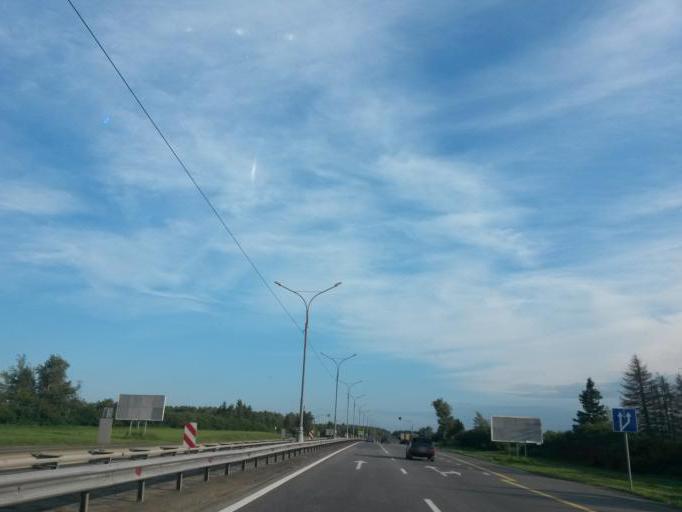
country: RU
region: Moskovskaya
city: Gorki-Leninskiye
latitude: 55.4737
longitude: 37.8529
